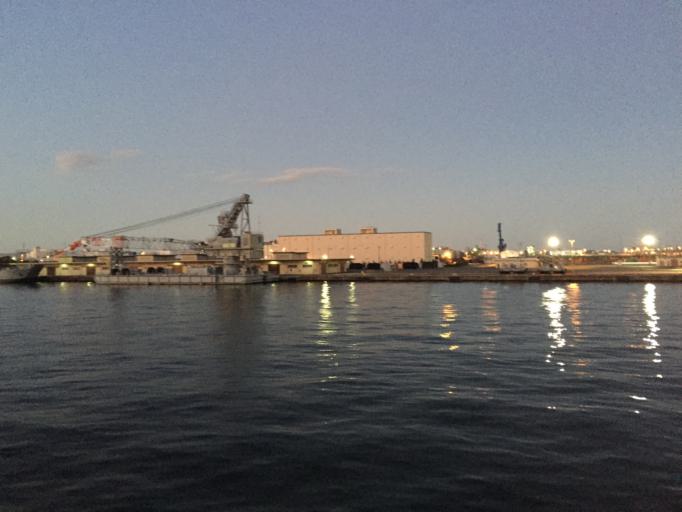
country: JP
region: Kanagawa
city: Yokohama
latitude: 35.4655
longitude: 139.6475
